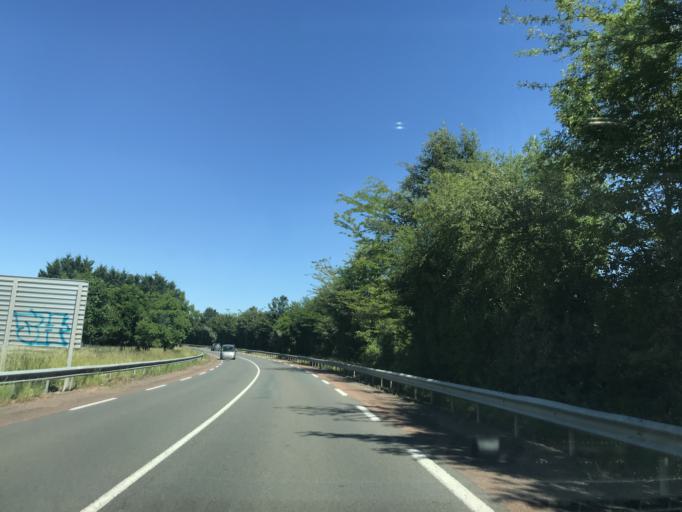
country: FR
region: Poitou-Charentes
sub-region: Departement de la Charente-Maritime
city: Gemozac
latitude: 45.5722
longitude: -0.6570
